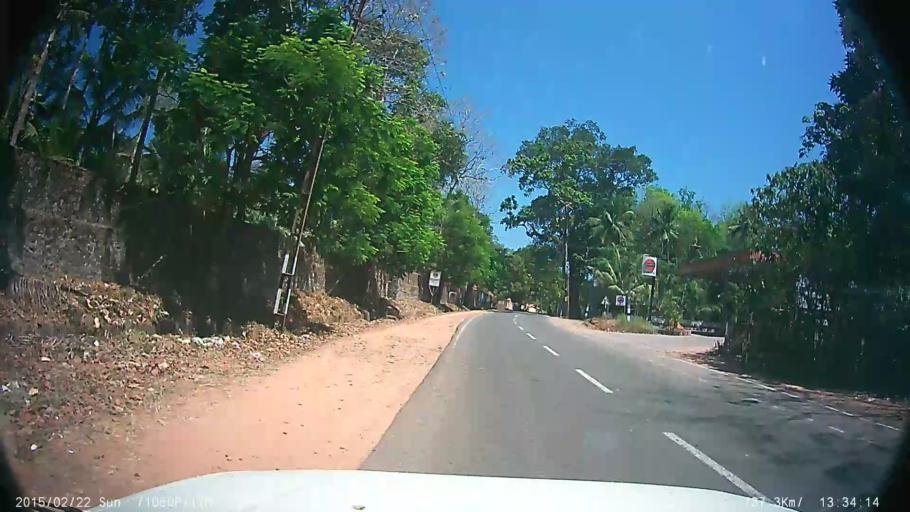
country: IN
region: Kerala
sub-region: Kottayam
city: Changanacheri
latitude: 9.4806
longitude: 76.5983
